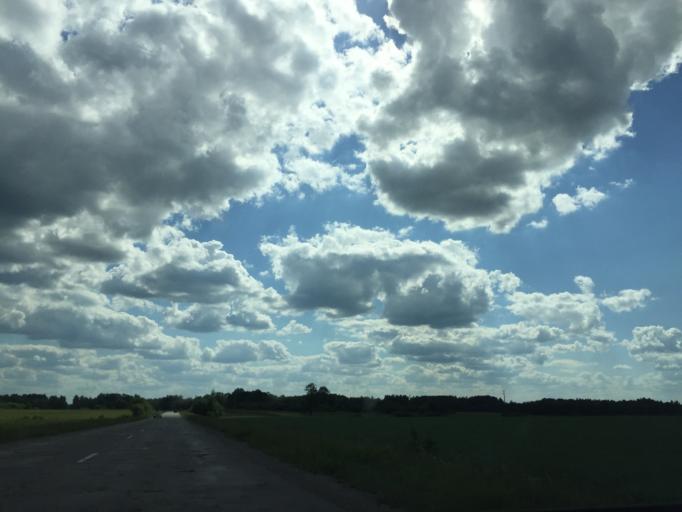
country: LV
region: Tukuma Rajons
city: Tukums
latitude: 56.8716
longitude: 23.0674
